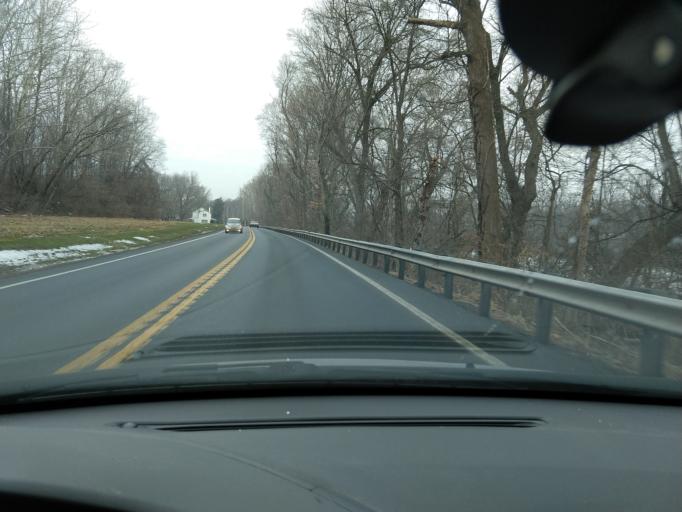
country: US
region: Pennsylvania
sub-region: Montgomery County
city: Stowe
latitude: 40.2422
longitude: -75.6989
